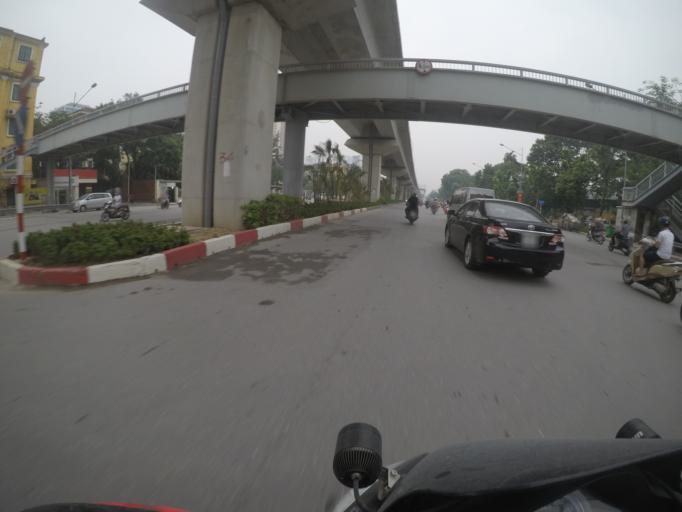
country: VN
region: Ha Noi
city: Thanh Xuan
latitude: 20.9947
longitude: 105.8079
